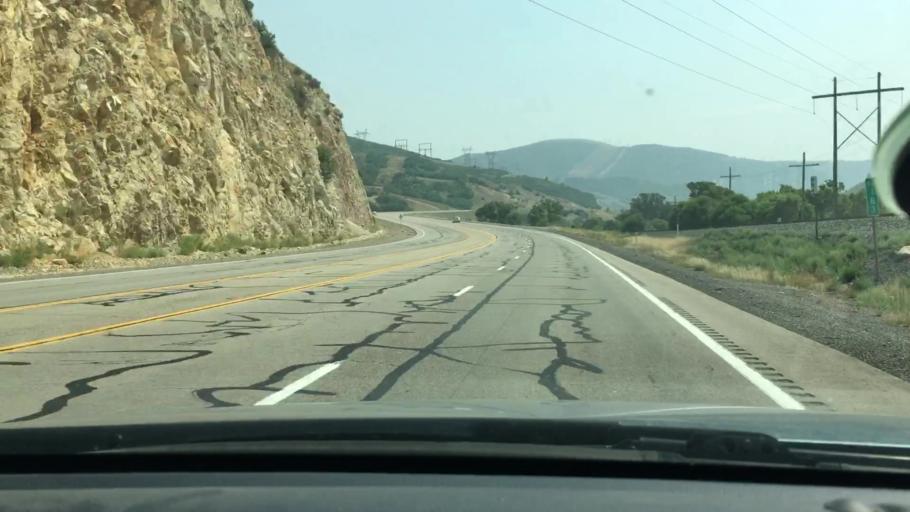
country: US
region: Utah
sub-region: Utah County
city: Mapleton
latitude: 40.0347
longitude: -111.5246
